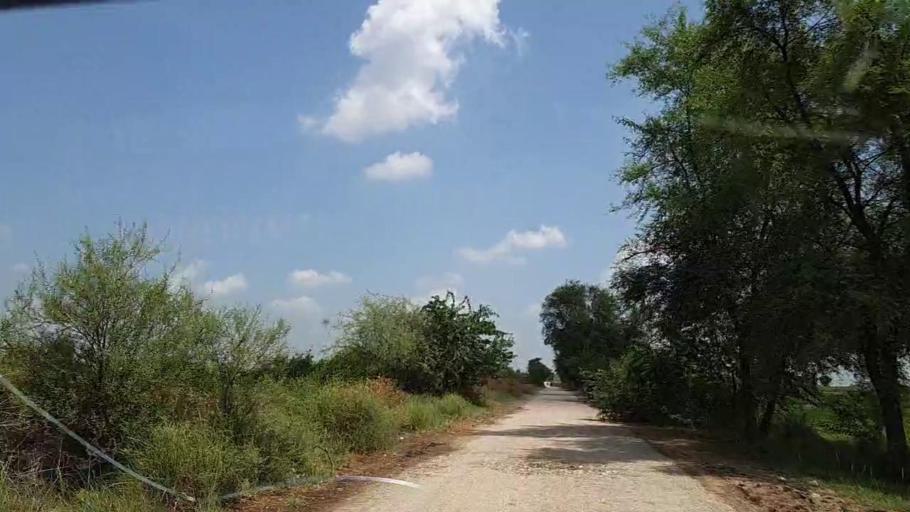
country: PK
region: Sindh
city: Tharu Shah
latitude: 26.9972
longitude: 68.0685
